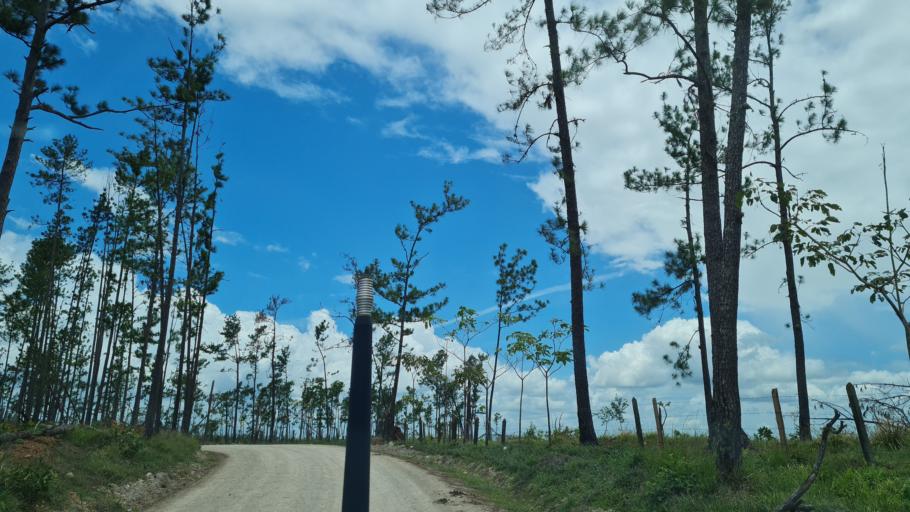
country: NI
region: Atlantico Sur
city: La Cruz de Rio Grande
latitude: 13.5715
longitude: -84.3220
